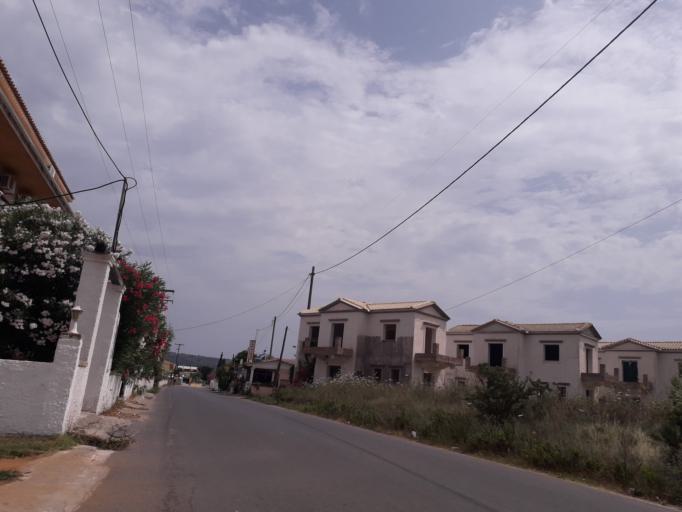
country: GR
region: Ionian Islands
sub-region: Nomos Kerkyras
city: Perivoli
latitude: 39.4266
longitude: 19.9478
